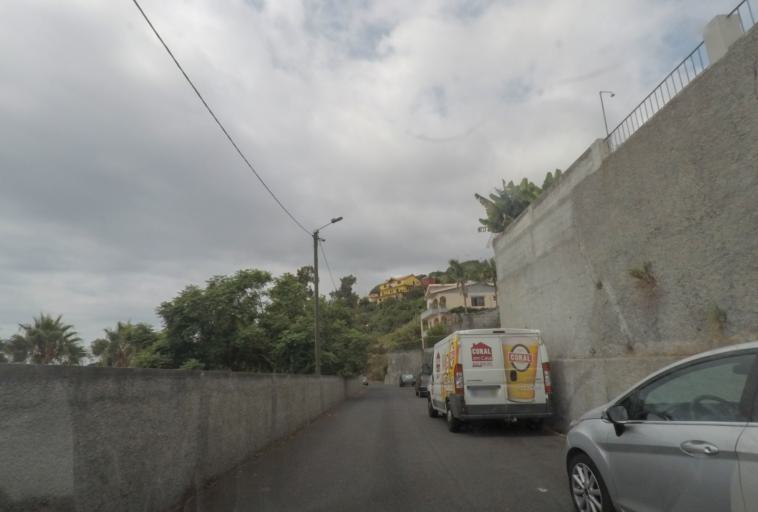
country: PT
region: Madeira
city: Camara de Lobos
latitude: 32.6466
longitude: -16.9499
